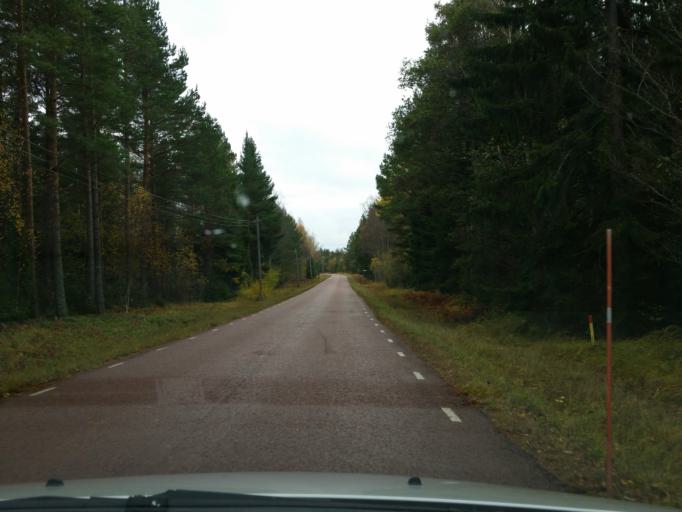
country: AX
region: Alands landsbygd
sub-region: Lemland
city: Lemland
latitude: 60.0025
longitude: 20.1868
